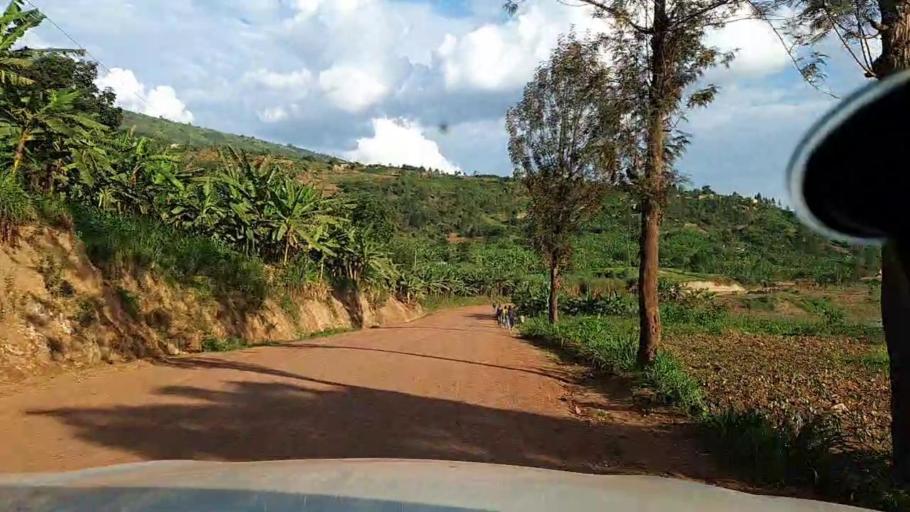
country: RW
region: Kigali
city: Kigali
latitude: -1.9305
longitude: 29.9944
